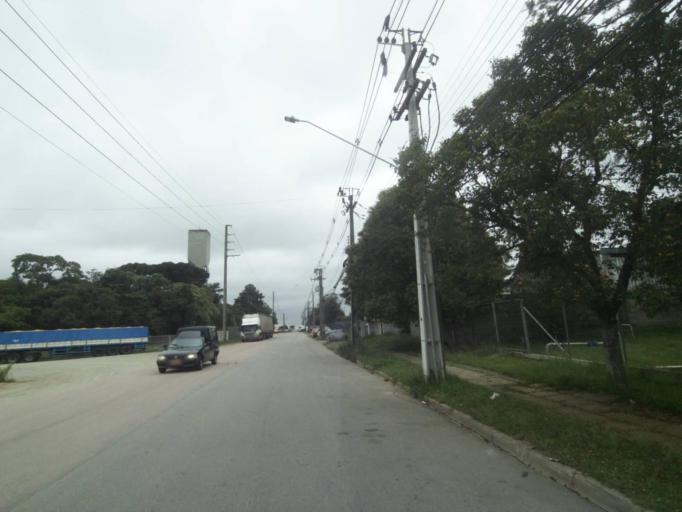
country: BR
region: Parana
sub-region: Sao Jose Dos Pinhais
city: Sao Jose dos Pinhais
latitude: -25.5572
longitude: -49.3095
